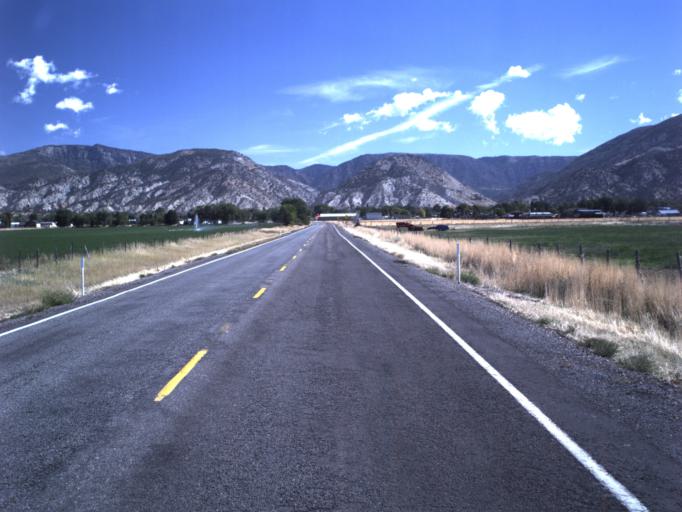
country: US
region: Utah
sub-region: Juab County
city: Nephi
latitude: 39.5583
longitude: -111.8780
